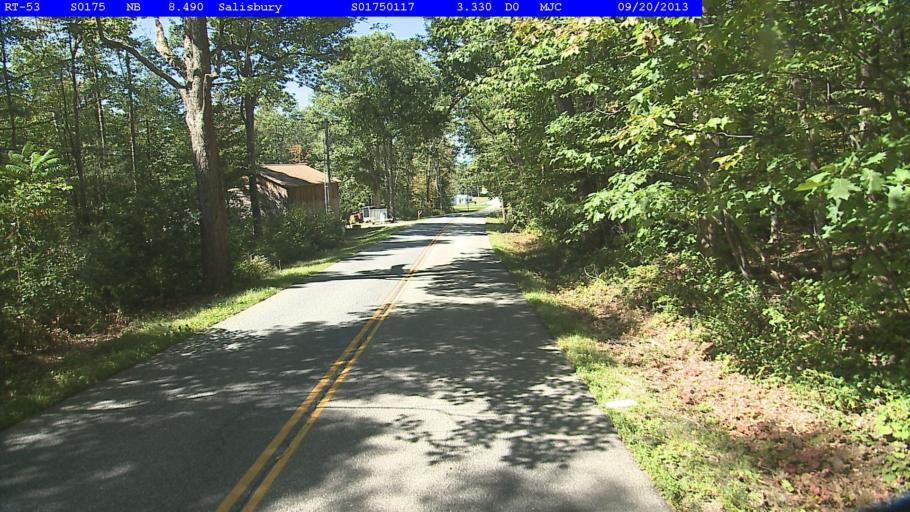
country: US
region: Vermont
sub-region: Addison County
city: Middlebury (village)
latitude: 43.9244
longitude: -73.0957
